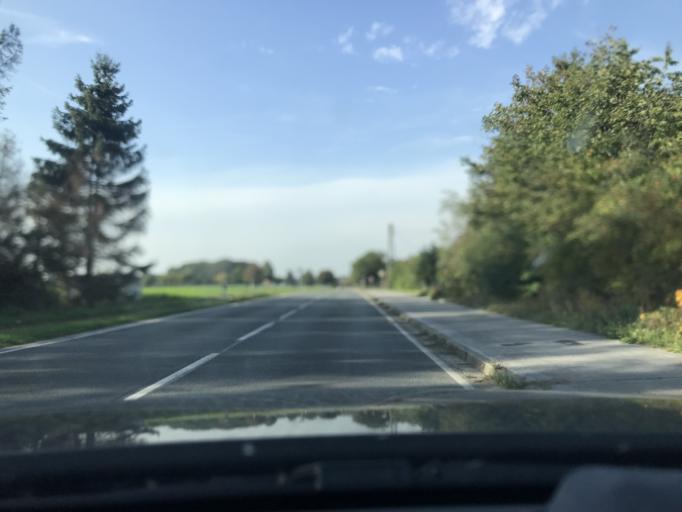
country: DE
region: North Rhine-Westphalia
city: Kalkar
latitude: 51.7302
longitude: 6.2729
